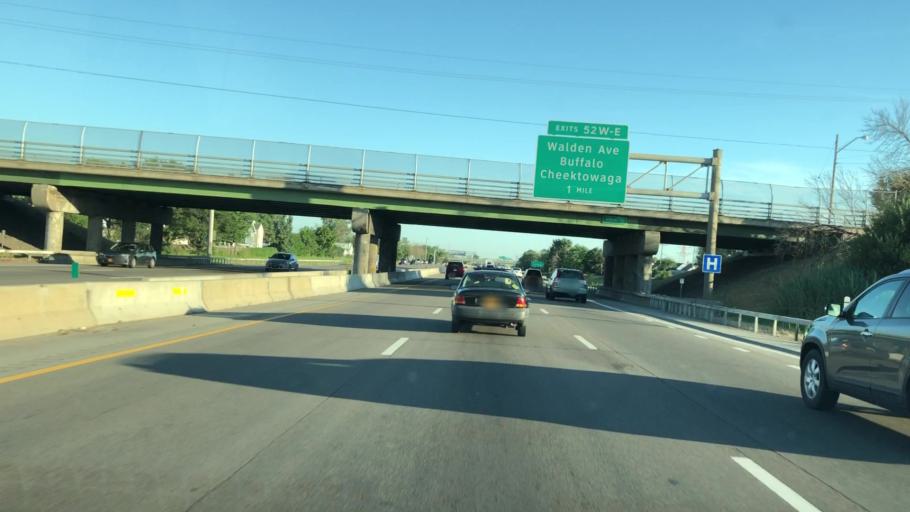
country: US
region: New York
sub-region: Erie County
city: Cheektowaga
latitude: 42.9254
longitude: -78.7664
